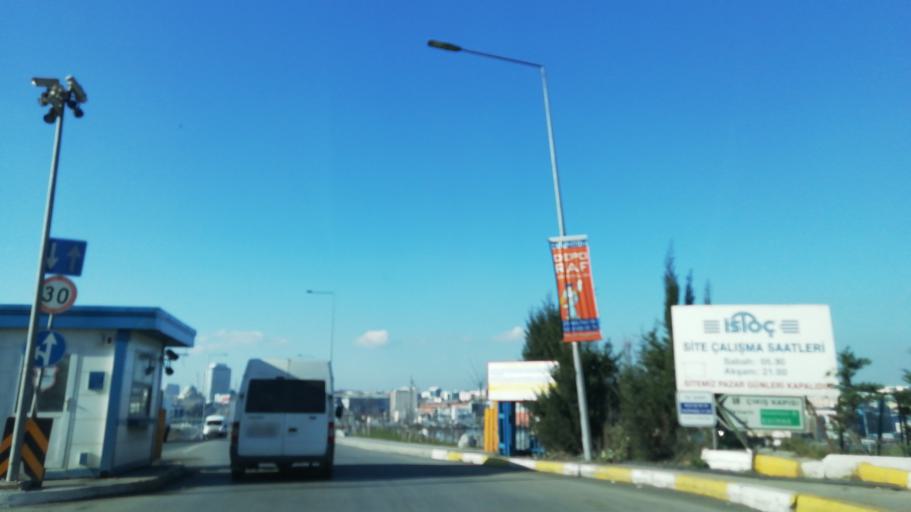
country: TR
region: Istanbul
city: Mahmutbey
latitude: 41.0708
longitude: 28.8198
